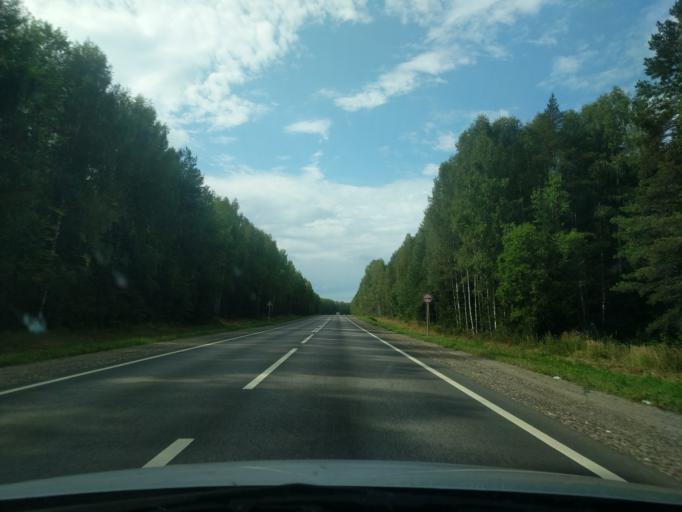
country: RU
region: Kostroma
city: Kadyy
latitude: 57.7976
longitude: 42.8630
